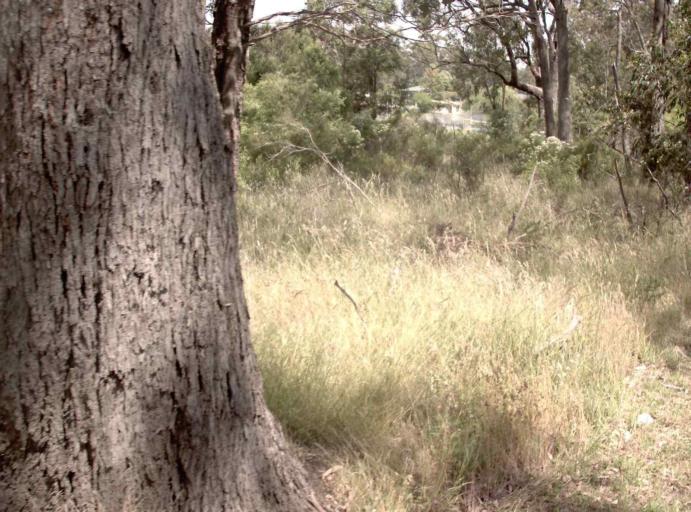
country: AU
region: Victoria
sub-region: Latrobe
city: Traralgon
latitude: -38.2948
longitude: 146.5384
